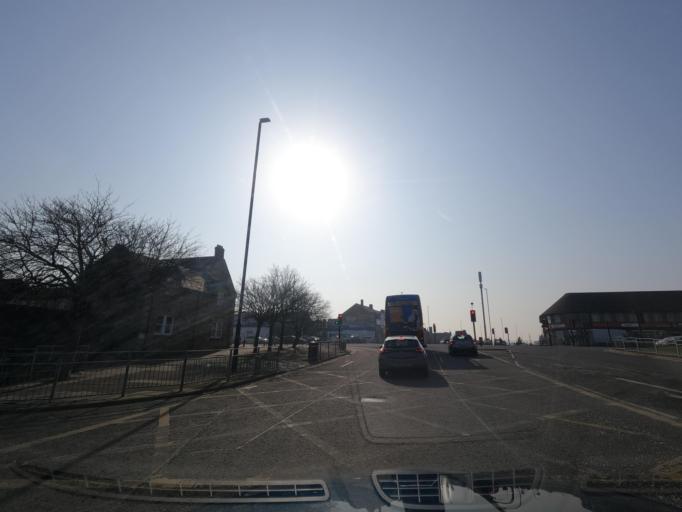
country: GB
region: England
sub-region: Newcastle upon Tyne
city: Gosforth
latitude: 55.0096
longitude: -1.5788
